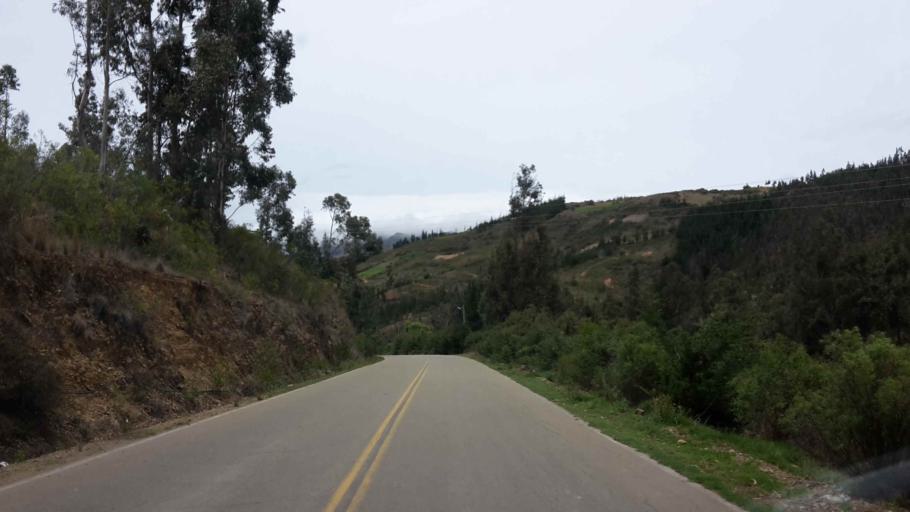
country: BO
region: Cochabamba
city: Totora
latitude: -17.6748
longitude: -65.2191
